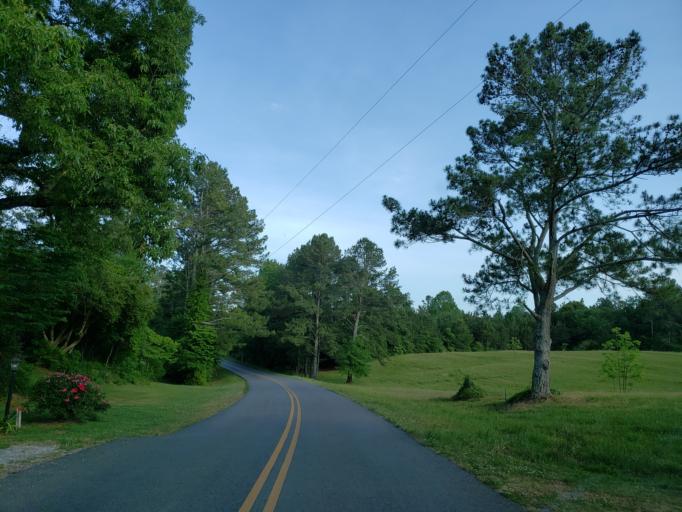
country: US
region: Georgia
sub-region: Carroll County
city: Bowdon
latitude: 33.4929
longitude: -85.3094
